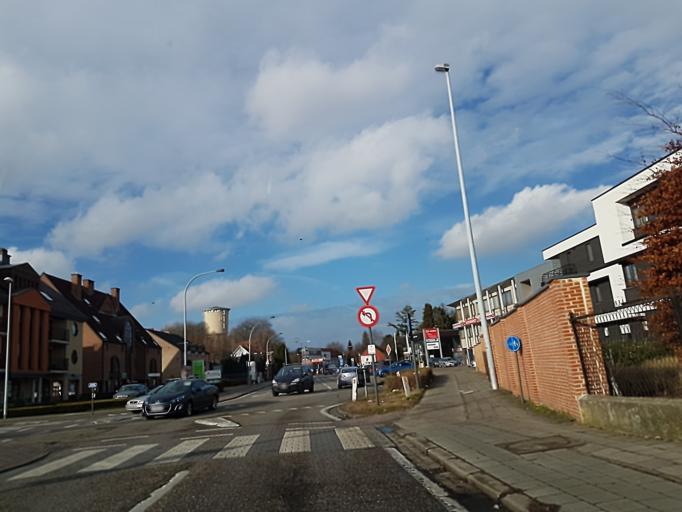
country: BE
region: Flanders
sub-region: Provincie Antwerpen
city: Mol
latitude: 51.1916
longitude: 5.1167
